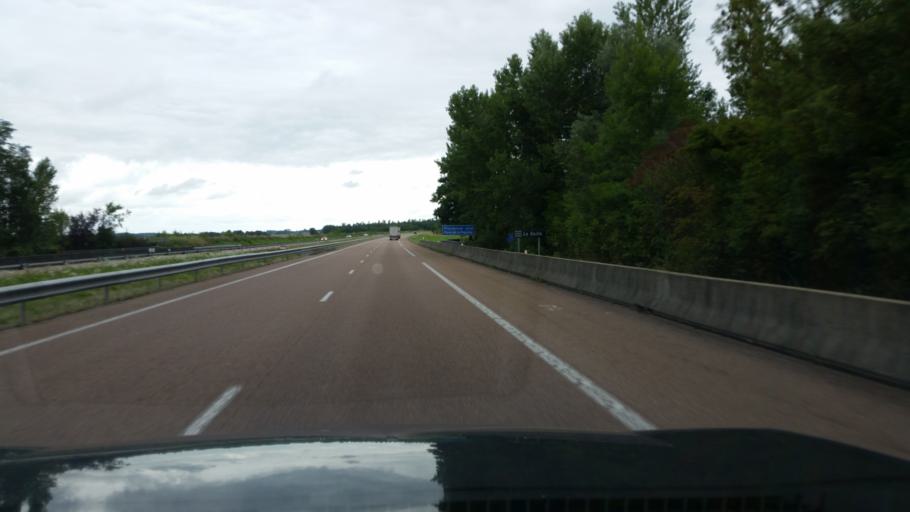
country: FR
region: Franche-Comte
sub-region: Departement du Jura
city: Bletterans
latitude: 46.7481
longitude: 5.5105
